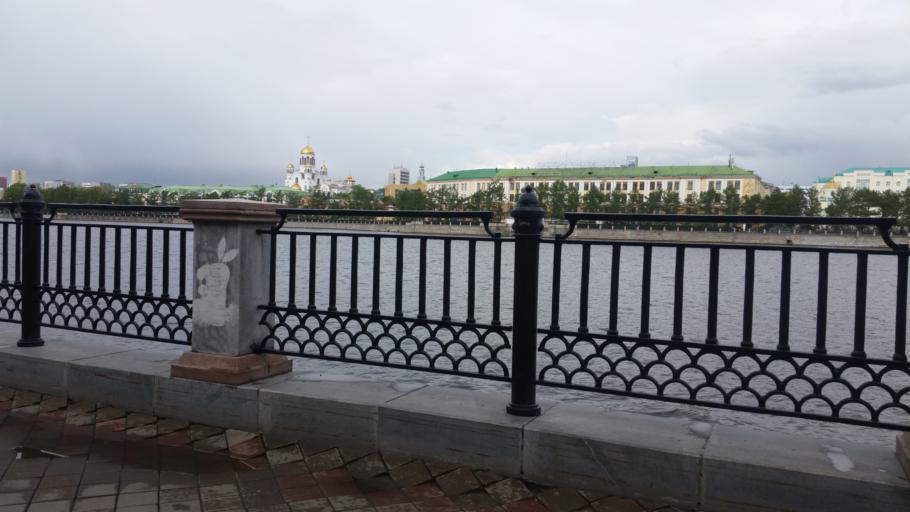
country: RU
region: Sverdlovsk
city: Yekaterinburg
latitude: 56.8396
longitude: 60.6011
